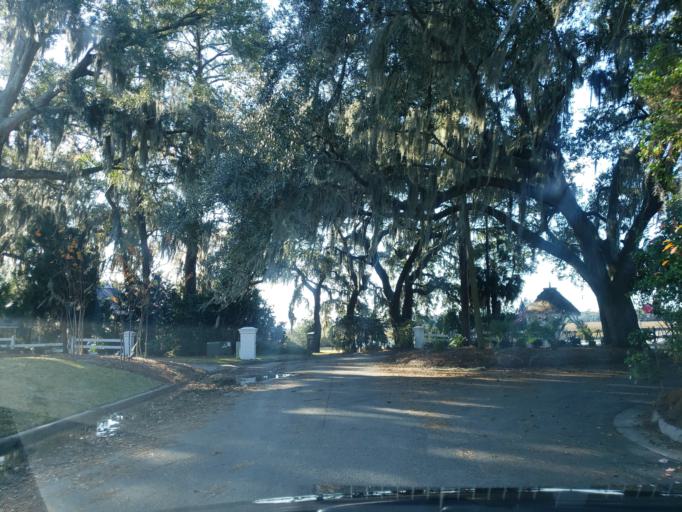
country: US
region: Georgia
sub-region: Chatham County
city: Thunderbolt
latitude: 32.0606
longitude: -81.0318
